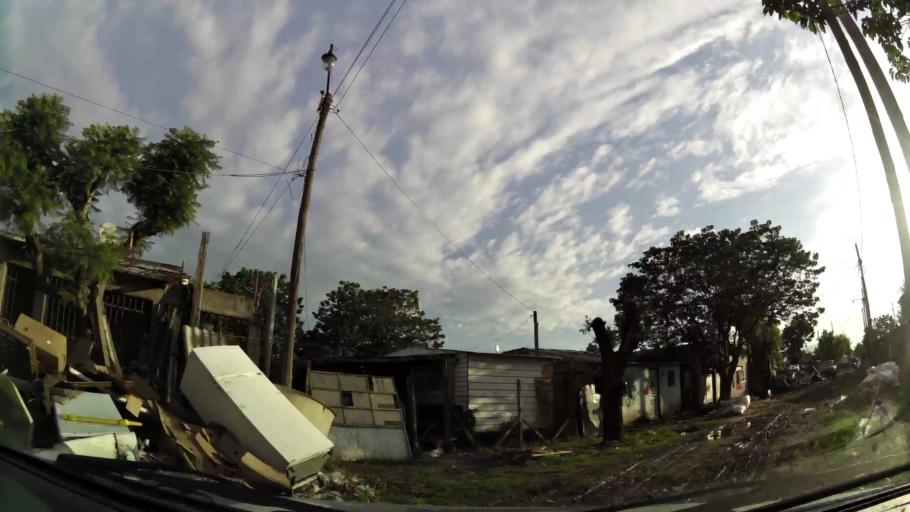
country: AR
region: Buenos Aires
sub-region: Partido de Lomas de Zamora
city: Lomas de Zamora
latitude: -34.7517
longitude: -58.3564
